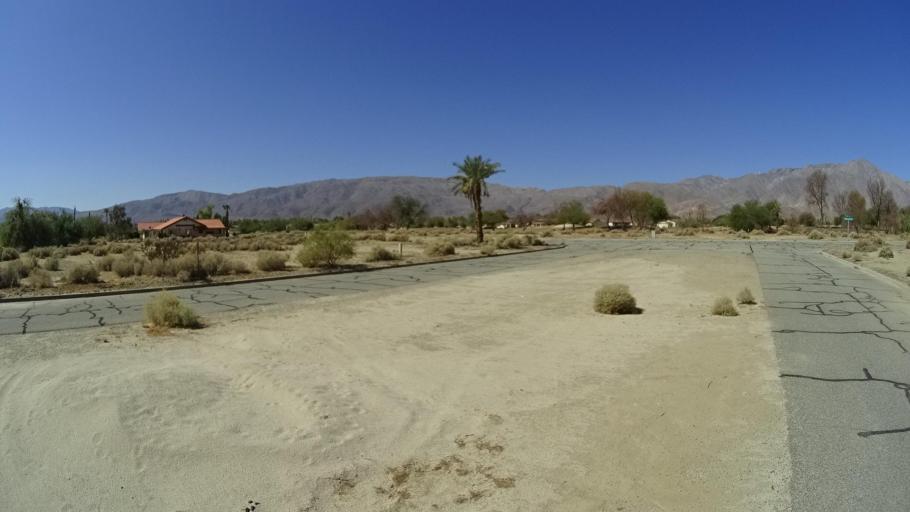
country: US
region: California
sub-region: San Diego County
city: Borrego Springs
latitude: 33.2439
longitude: -116.3507
